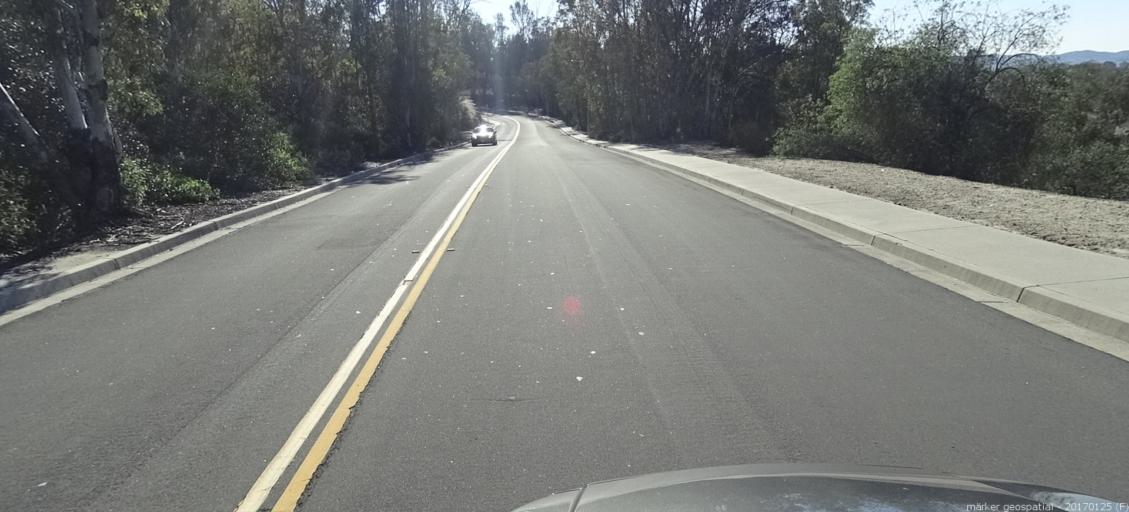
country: US
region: California
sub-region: Orange County
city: Lake Forest
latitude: 33.6514
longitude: -117.6809
